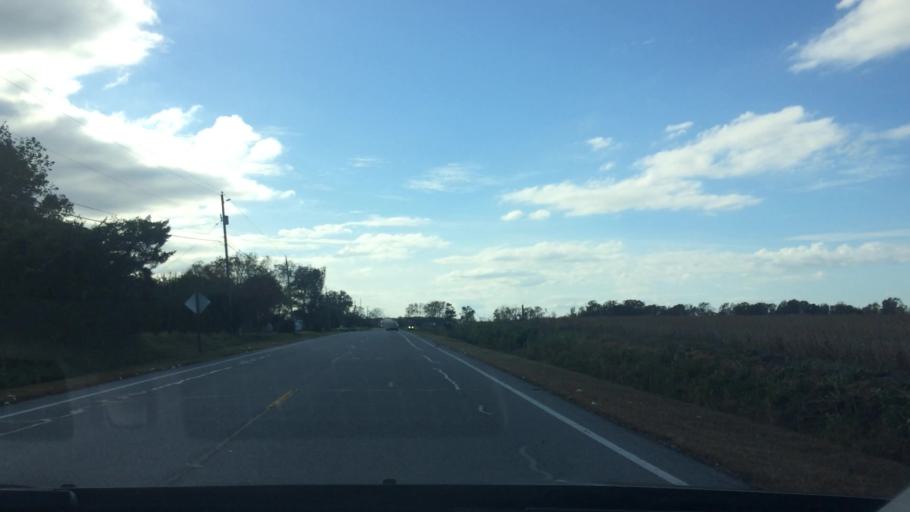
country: US
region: North Carolina
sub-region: Greene County
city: Snow Hill
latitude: 35.4378
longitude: -77.7622
